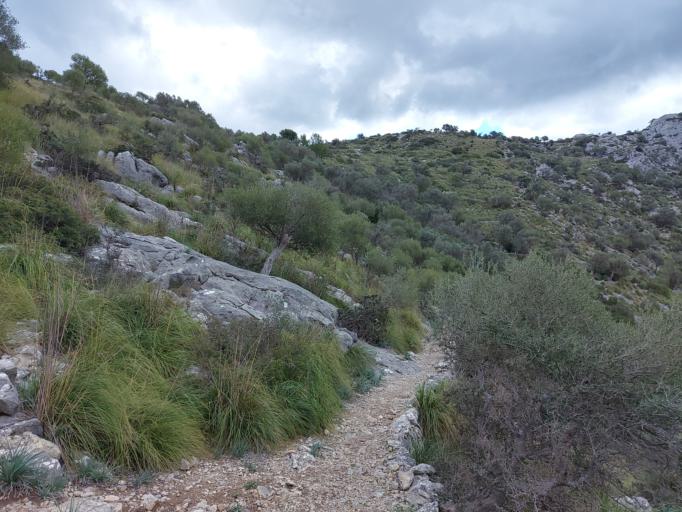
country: ES
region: Balearic Islands
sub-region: Illes Balears
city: Mancor de la Vall
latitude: 39.7696
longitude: 2.8194
